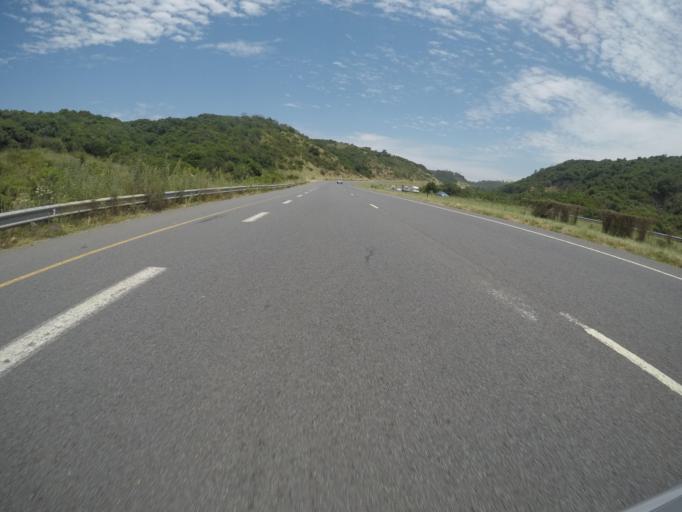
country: ZA
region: Eastern Cape
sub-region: Buffalo City Metropolitan Municipality
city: East London
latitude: -32.9671
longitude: 27.9168
